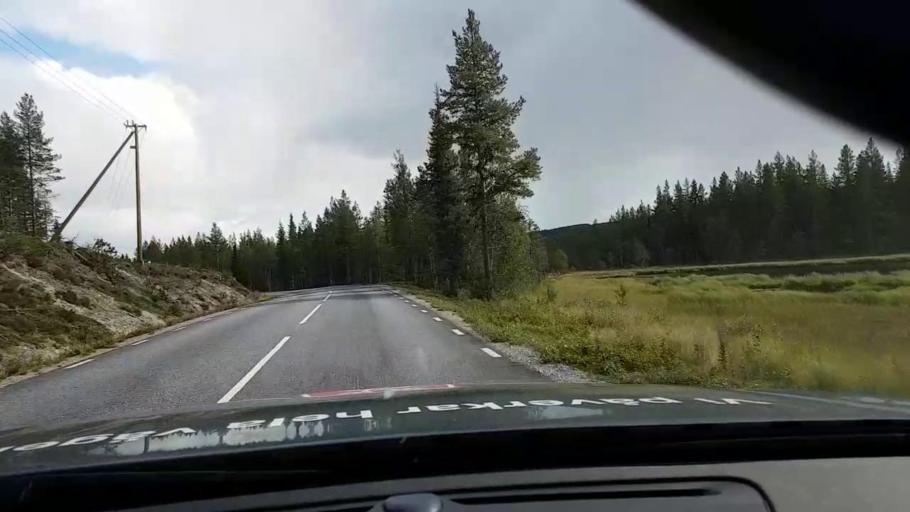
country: SE
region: Vaesterbotten
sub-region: Asele Kommun
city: Asele
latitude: 63.8489
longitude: 17.4033
